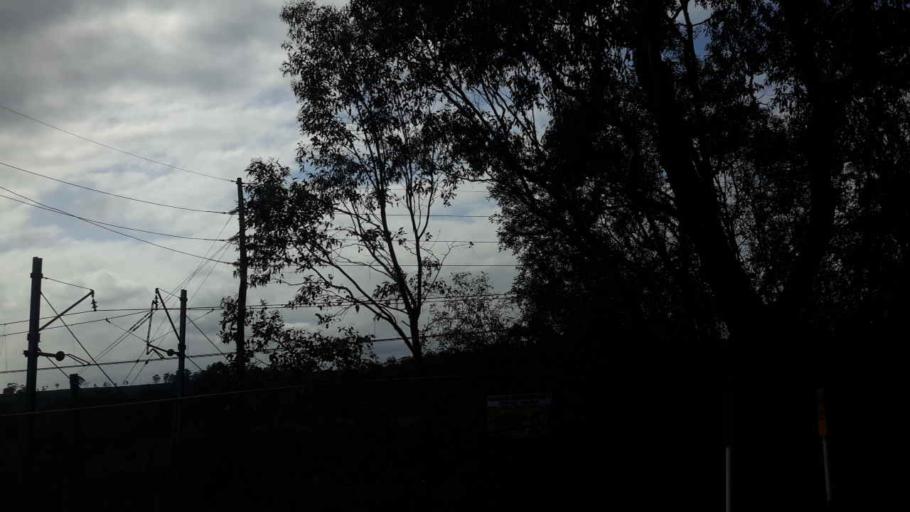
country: AU
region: New South Wales
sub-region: Campbelltown Municipality
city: Glen Alpine
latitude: -34.0807
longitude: 150.7804
